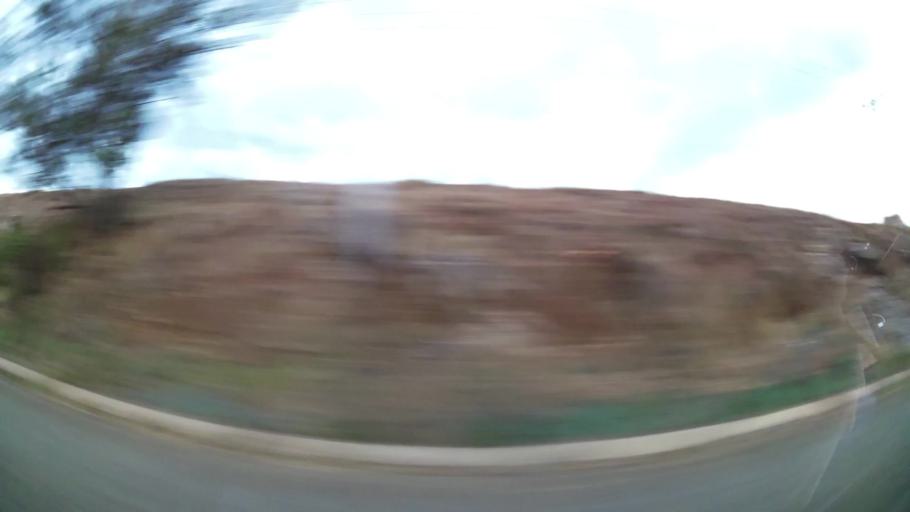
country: ZA
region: Gauteng
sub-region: West Rand District Municipality
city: Krugersdorp
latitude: -26.0380
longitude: 27.7226
